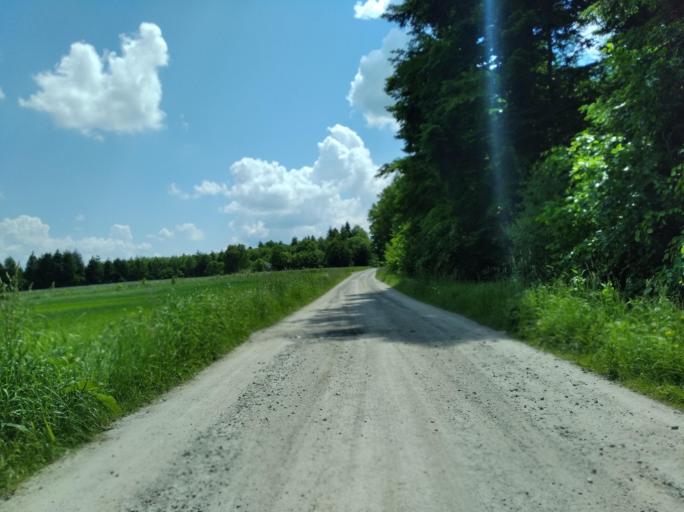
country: PL
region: Subcarpathian Voivodeship
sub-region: Powiat ropczycko-sedziszowski
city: Zagorzyce
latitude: 49.9702
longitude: 21.6908
